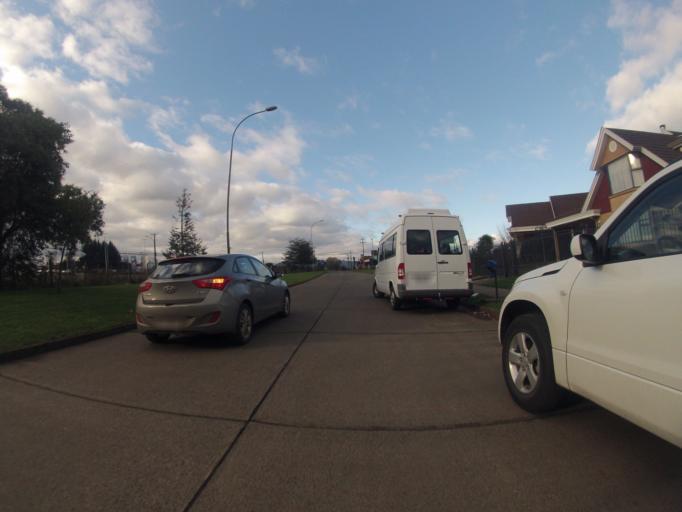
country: CL
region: Araucania
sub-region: Provincia de Cautin
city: Temuco
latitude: -38.7359
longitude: -72.6410
